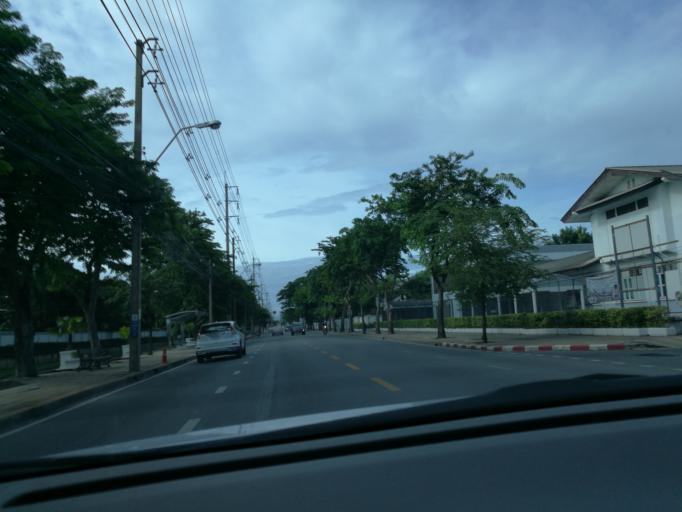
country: TH
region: Bangkok
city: Bang Sue
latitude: 13.7960
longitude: 100.5313
